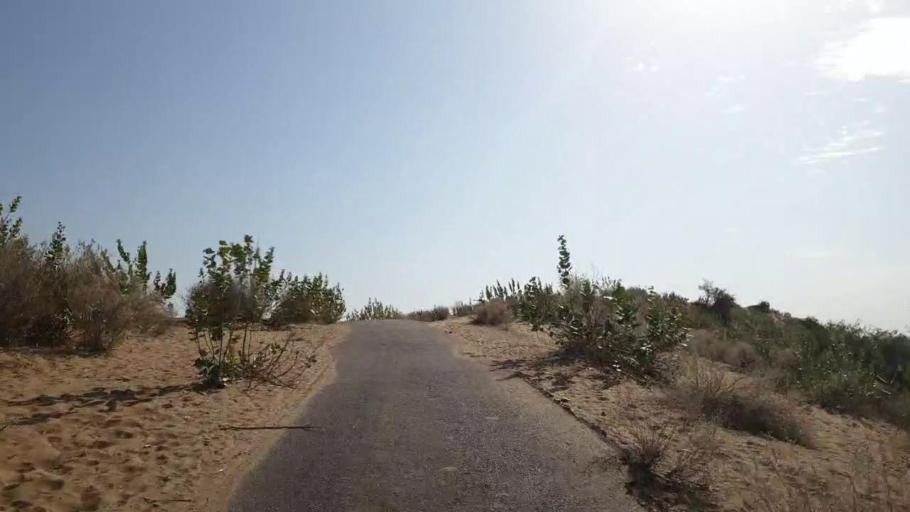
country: PK
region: Sindh
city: Nabisar
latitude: 25.0560
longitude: 70.0233
